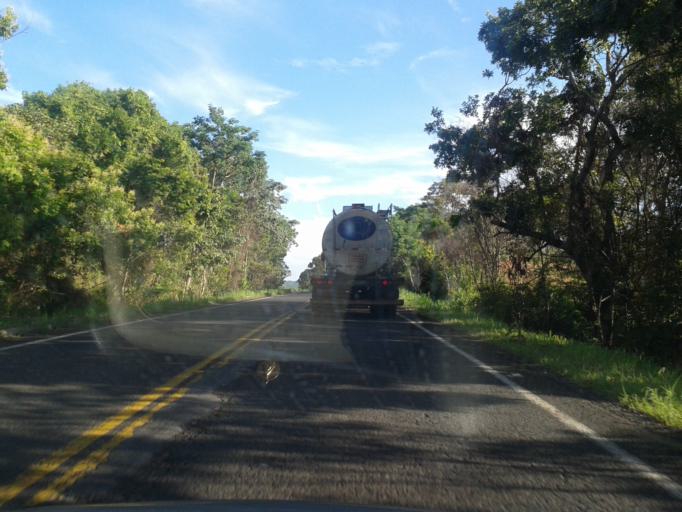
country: BR
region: Minas Gerais
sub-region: Tupaciguara
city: Tupaciguara
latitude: -18.2237
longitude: -48.5727
